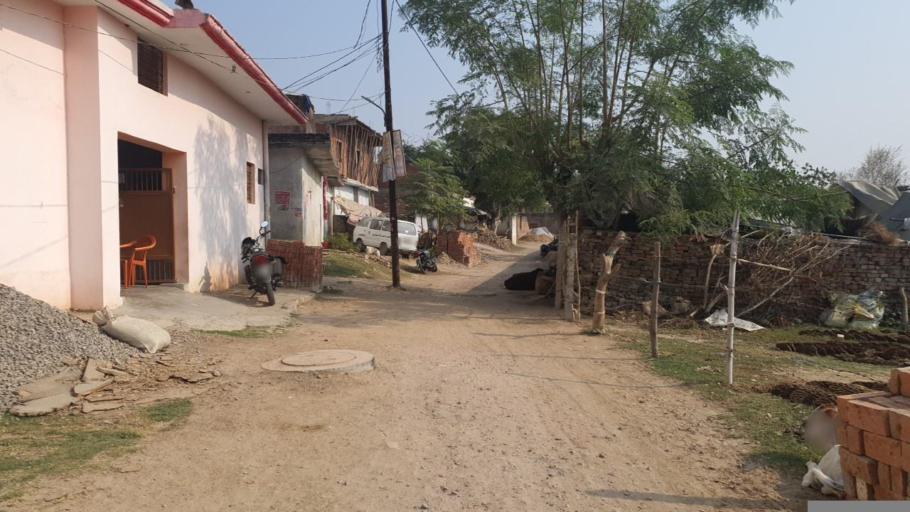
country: IN
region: Uttar Pradesh
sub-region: Lucknow District
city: Lucknow
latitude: 26.7976
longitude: 81.0069
